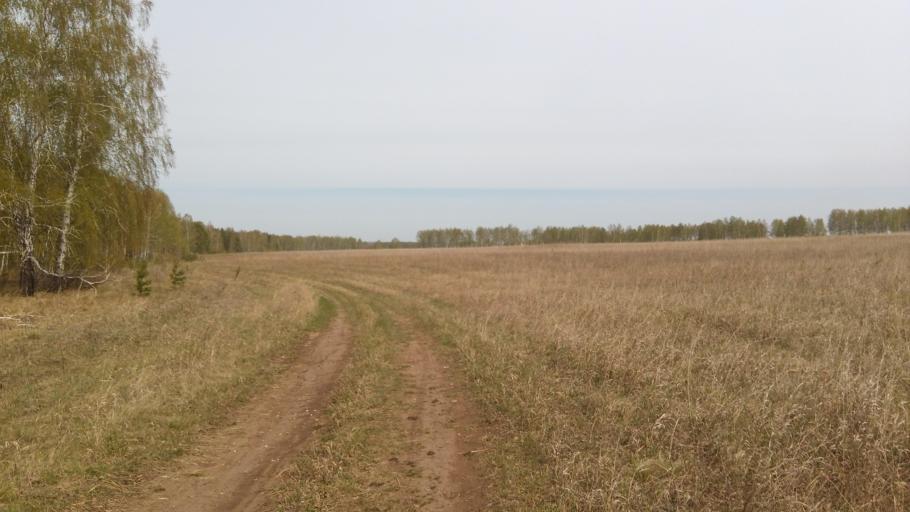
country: RU
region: Chelyabinsk
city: Timiryazevskiy
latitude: 55.0153
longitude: 60.8625
